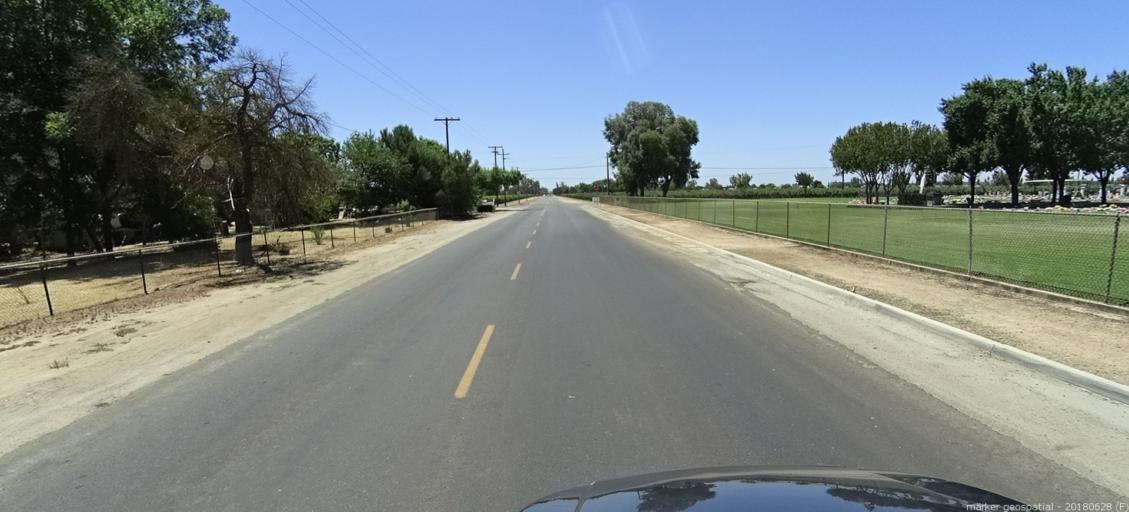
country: US
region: California
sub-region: Madera County
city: Parksdale
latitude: 36.9537
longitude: -120.0286
